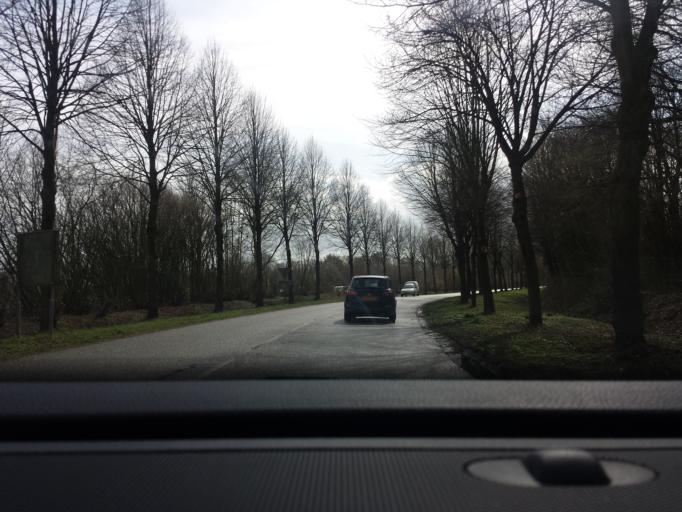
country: NL
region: Gelderland
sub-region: Oude IJsselstreek
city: Varsseveld
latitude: 51.9502
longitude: 6.4596
